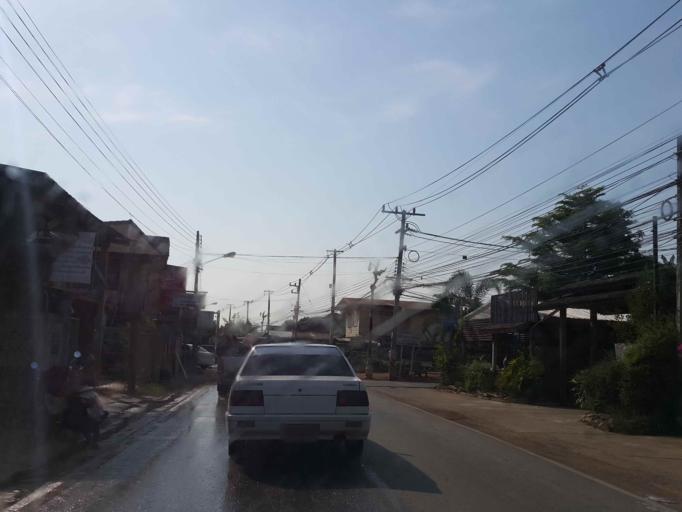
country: TH
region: Sukhothai
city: Thung Saliam
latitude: 17.3186
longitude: 99.5483
